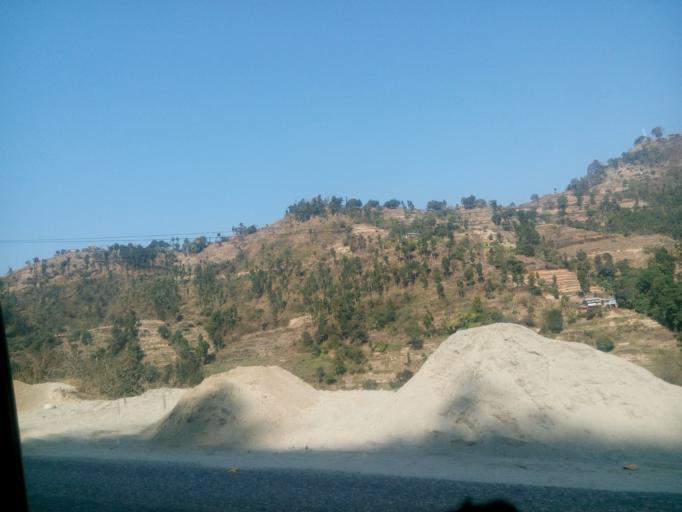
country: NP
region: Central Region
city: Kirtipur
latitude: 27.7537
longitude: 85.0623
